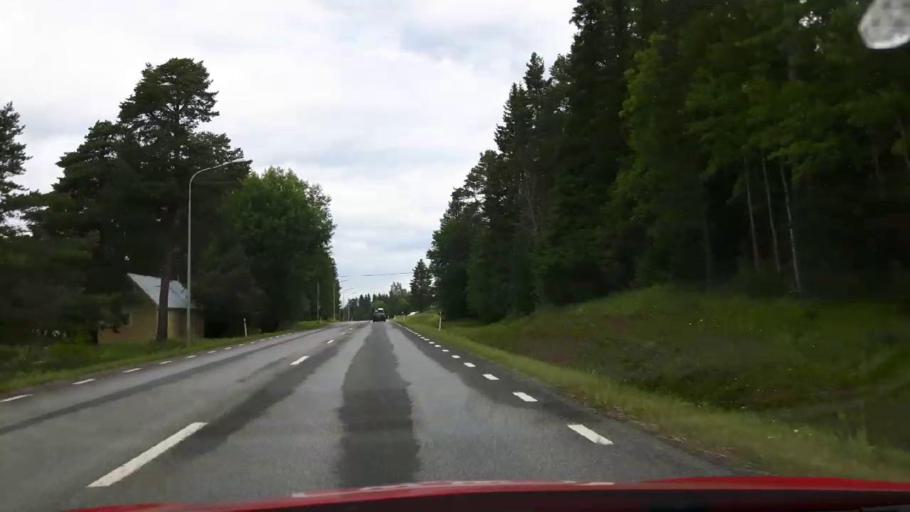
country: SE
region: Jaemtland
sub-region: Stroemsunds Kommun
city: Stroemsund
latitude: 63.6615
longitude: 15.3886
